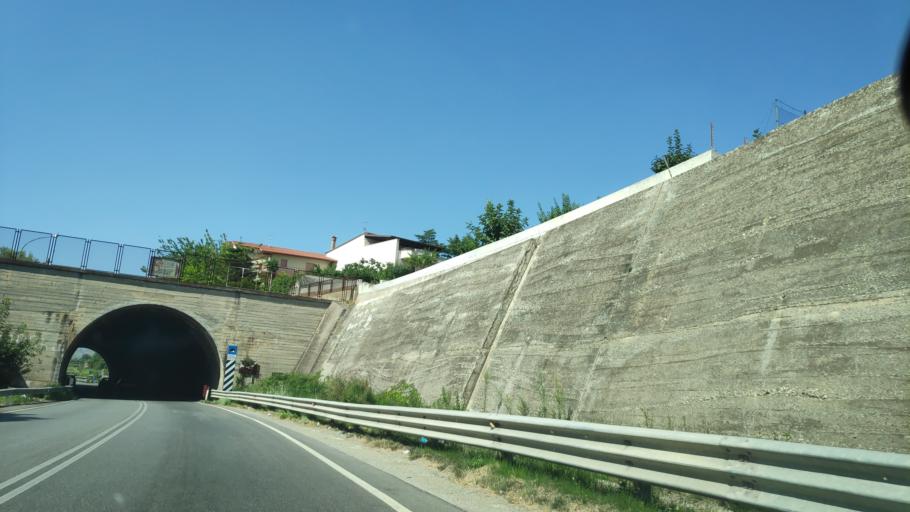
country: IT
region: Calabria
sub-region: Provincia di Reggio Calabria
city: Bovalino
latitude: 38.1526
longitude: 16.1713
